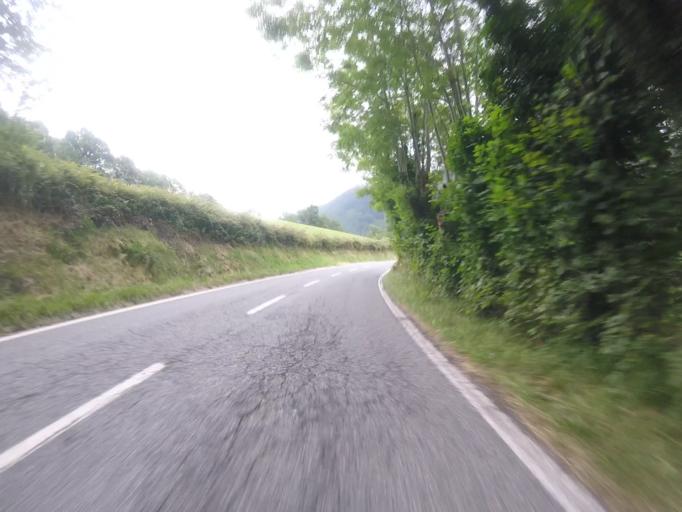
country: ES
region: Navarre
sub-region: Provincia de Navarra
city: Ezkurra
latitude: 43.0852
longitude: -1.8439
